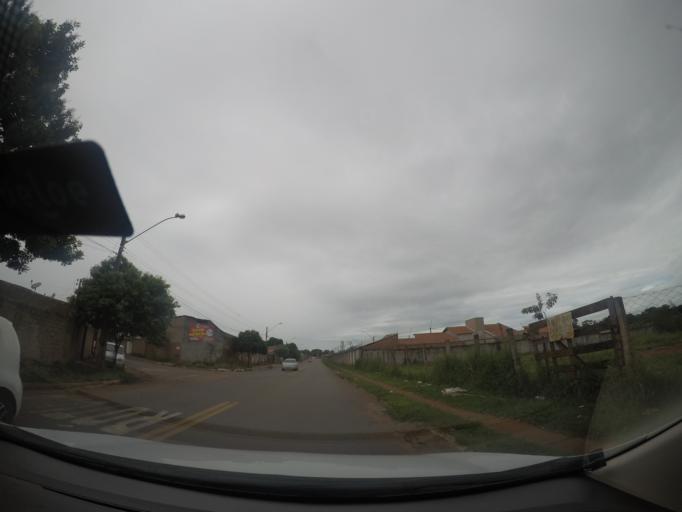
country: BR
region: Goias
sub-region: Goiania
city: Goiania
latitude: -16.6084
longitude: -49.3477
